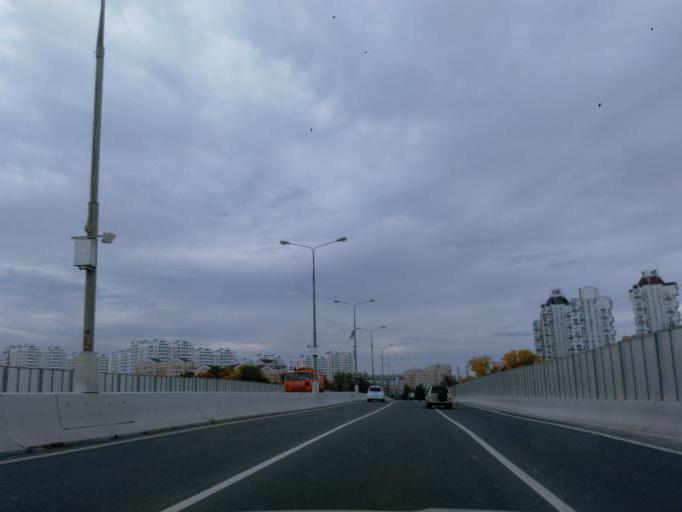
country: RU
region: Moscow
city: Zelenograd
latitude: 55.9802
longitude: 37.1725
